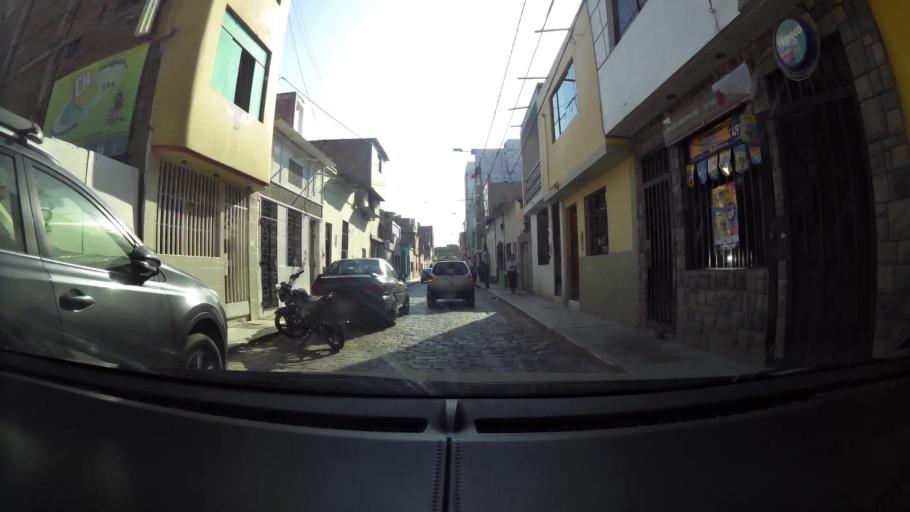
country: PE
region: Lambayeque
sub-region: Provincia de Chiclayo
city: Chiclayo
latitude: -6.7742
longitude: -79.8412
